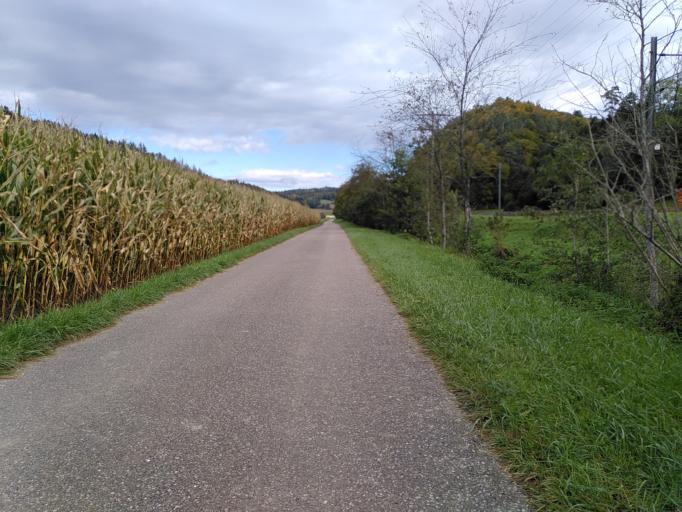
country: CH
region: Bern
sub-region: Emmental District
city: Wynigen
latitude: 47.1145
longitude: 7.6677
